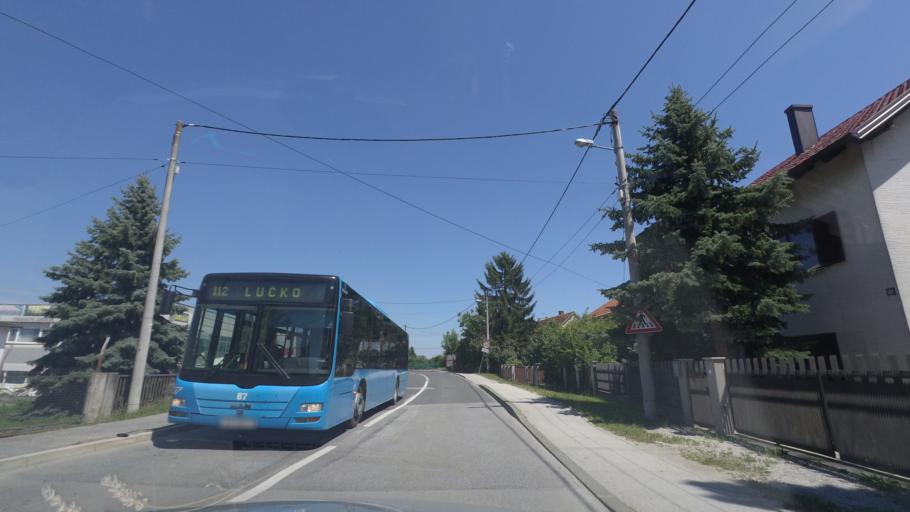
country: HR
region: Grad Zagreb
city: Zadvorsko
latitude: 45.7648
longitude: 15.9250
